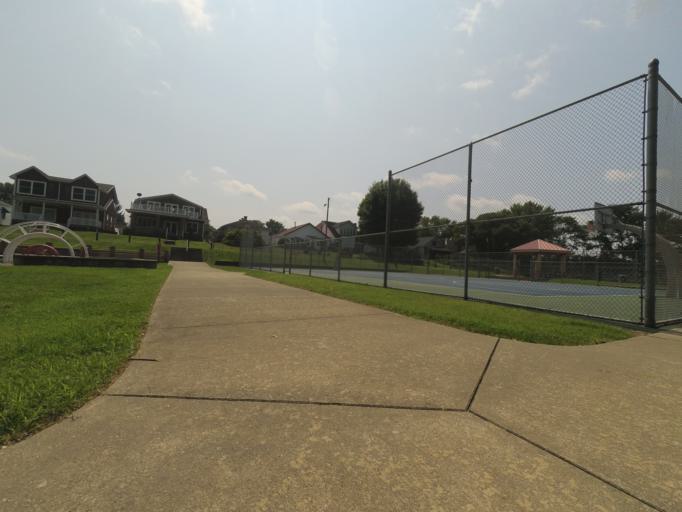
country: US
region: West Virginia
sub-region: Cabell County
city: Huntington
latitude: 38.4355
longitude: -82.4070
